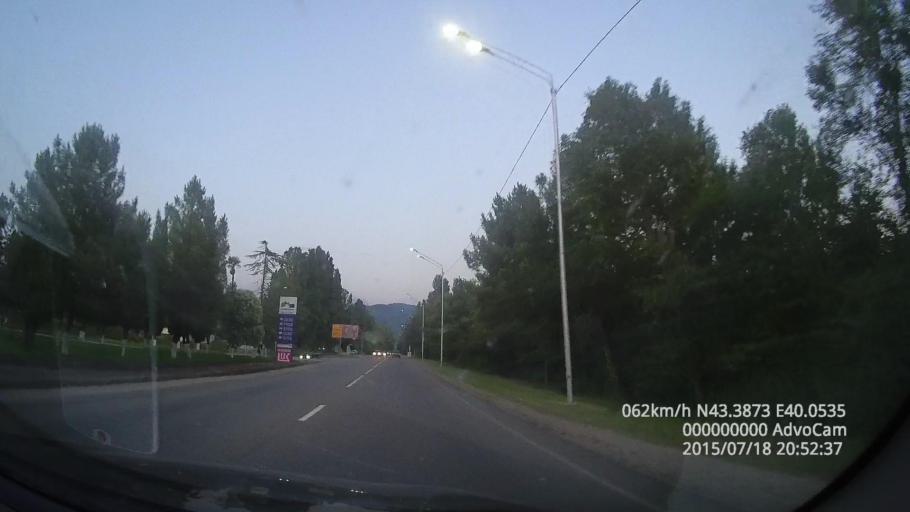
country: GE
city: Gantiadi
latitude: 43.3871
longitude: 40.0550
